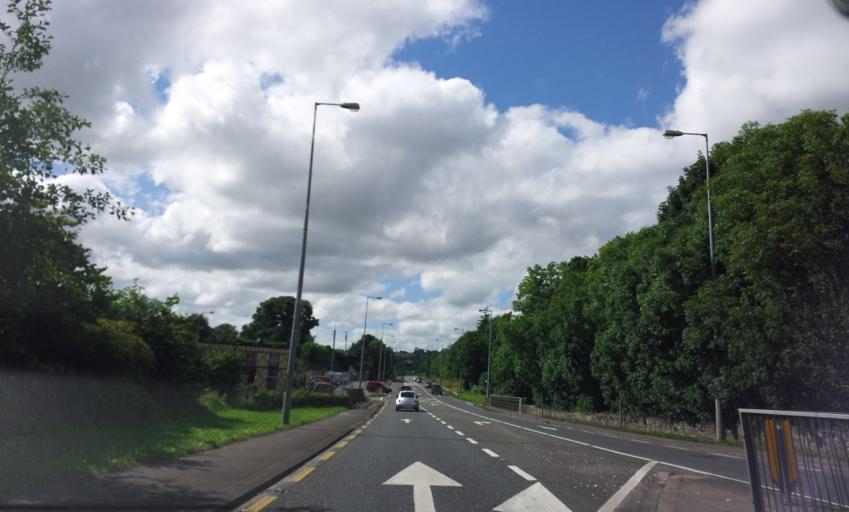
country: IE
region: Munster
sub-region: County Cork
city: Killumney
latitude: 51.8802
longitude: -8.6532
